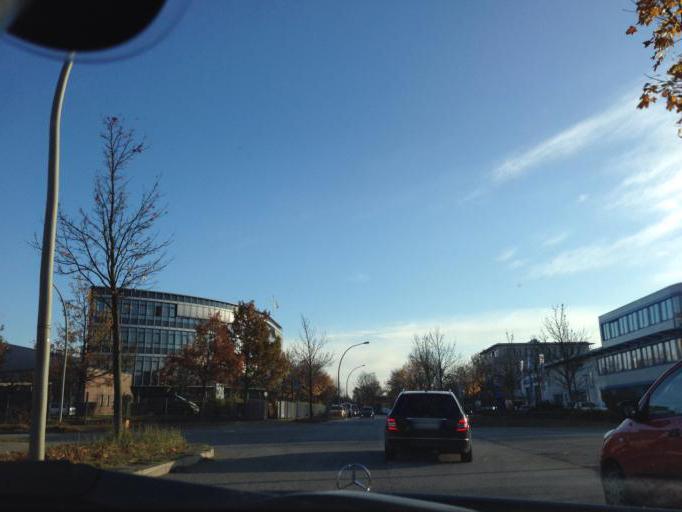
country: DE
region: Schleswig-Holstein
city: Stapelfeld
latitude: 53.6094
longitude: 10.1847
